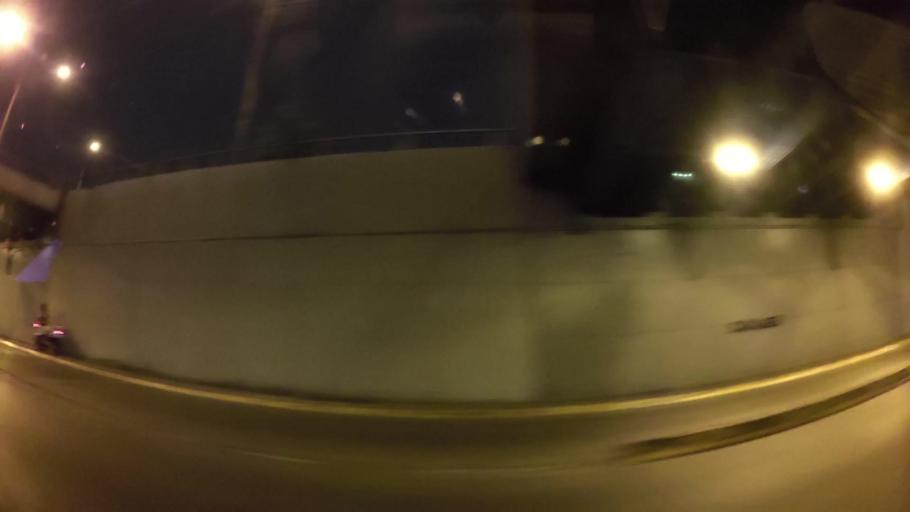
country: PE
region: Lima
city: Lima
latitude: -12.0769
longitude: -77.0290
